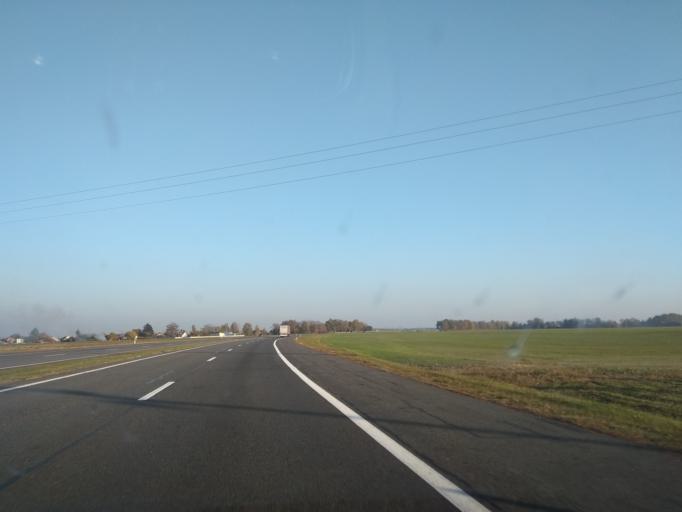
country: BY
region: Brest
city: Kobryn
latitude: 52.1990
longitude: 24.2936
